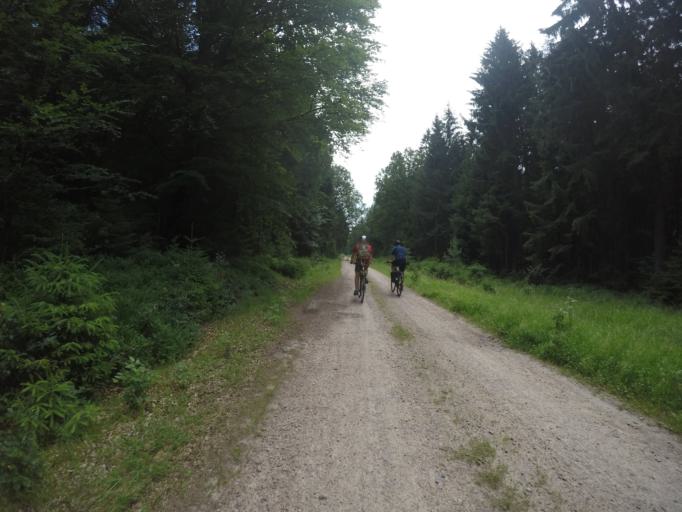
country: DE
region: Lower Saxony
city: Undeloh
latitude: 53.2394
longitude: 9.9618
